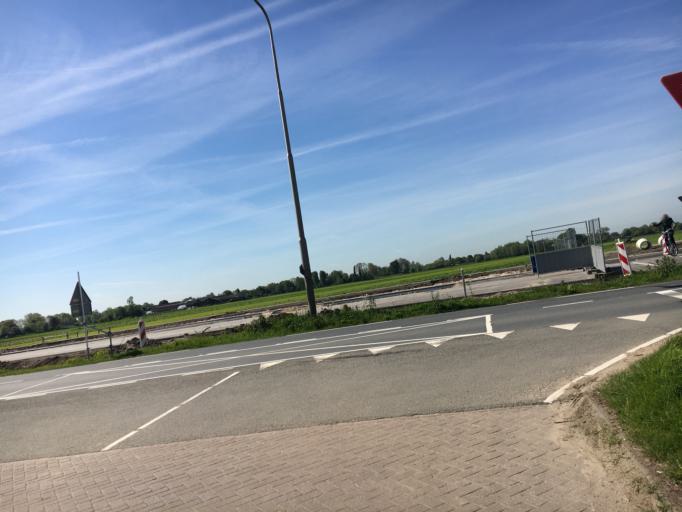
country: NL
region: North Holland
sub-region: Gemeente Weesp
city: Weesp
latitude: 52.2928
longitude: 5.0683
